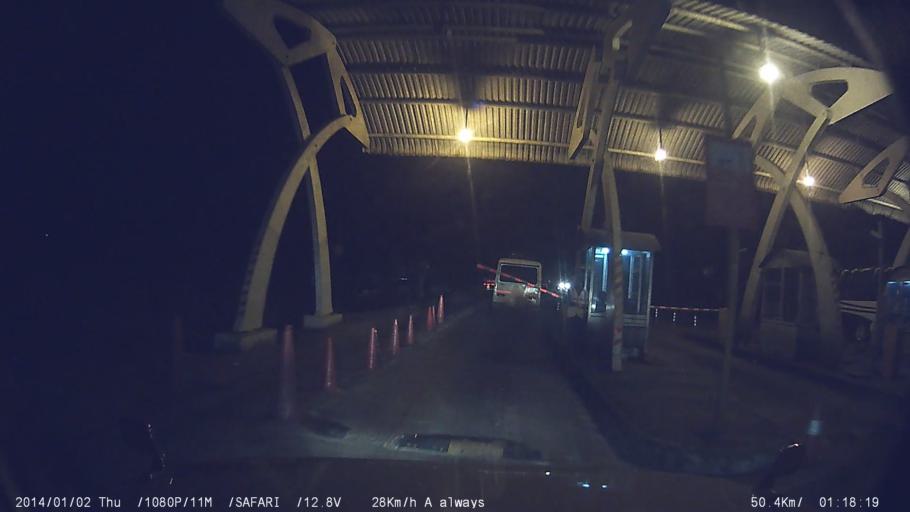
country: IN
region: Tamil Nadu
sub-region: Coimbatore
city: Irugur
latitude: 11.0127
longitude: 77.0730
